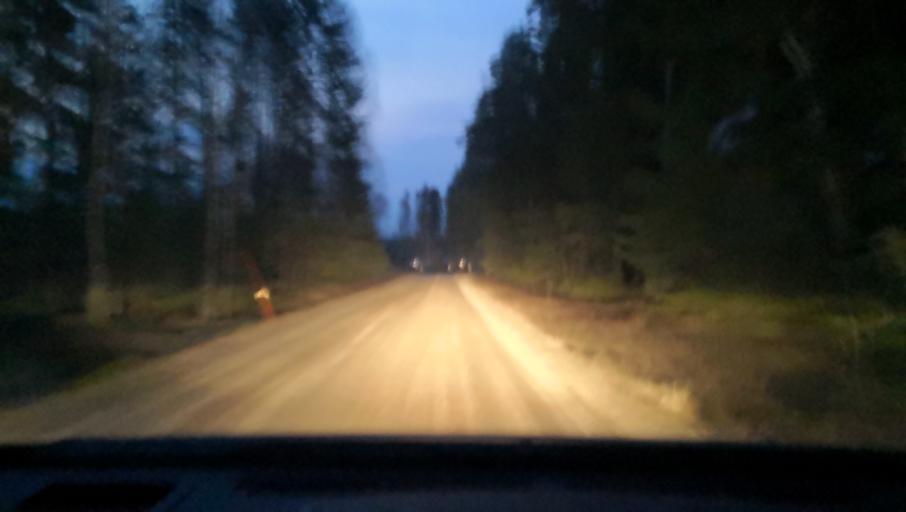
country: SE
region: OErebro
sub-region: Lindesbergs Kommun
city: Frovi
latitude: 59.5910
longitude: 15.4699
